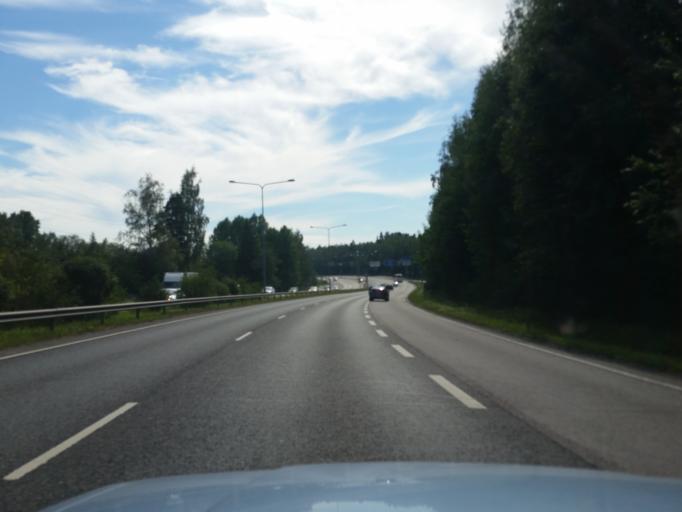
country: FI
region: Uusimaa
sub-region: Helsinki
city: Otaniemi
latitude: 60.2020
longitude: 24.8127
